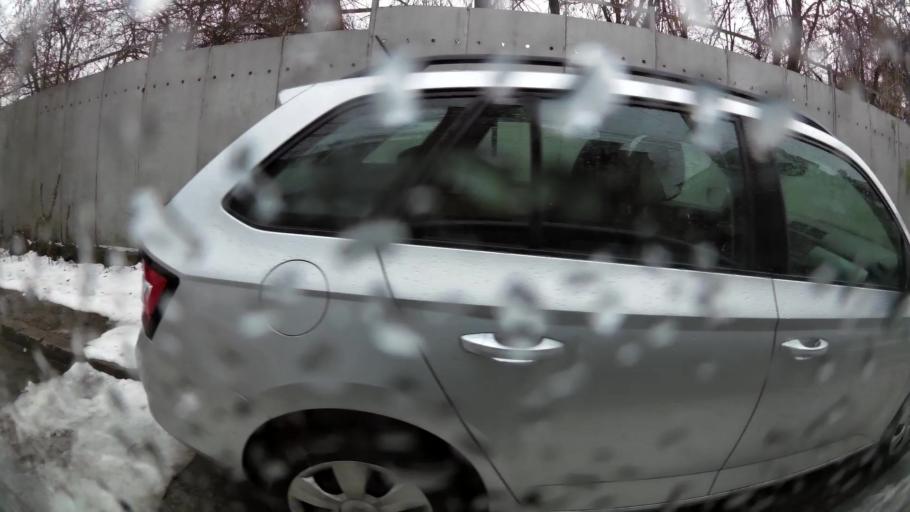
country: BG
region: Sofia-Capital
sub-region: Stolichna Obshtina
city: Sofia
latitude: 42.6743
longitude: 23.2664
